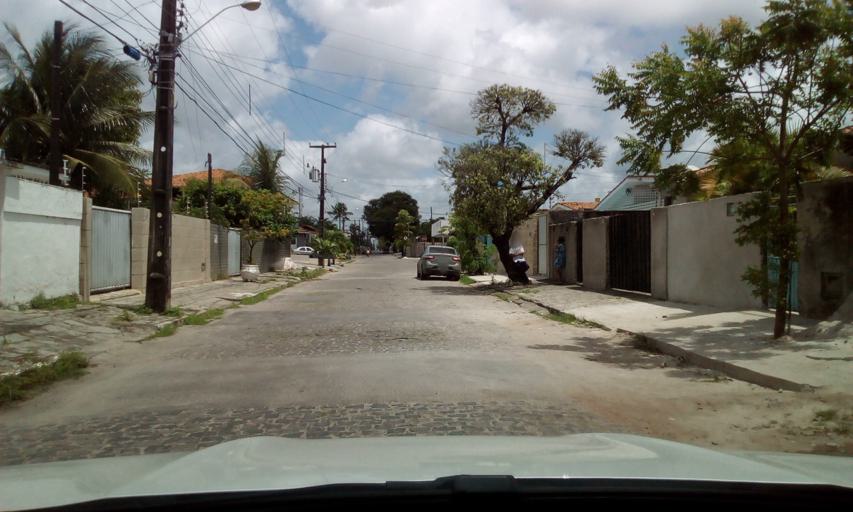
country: BR
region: Paraiba
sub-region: Joao Pessoa
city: Joao Pessoa
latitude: -7.1640
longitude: -34.8684
